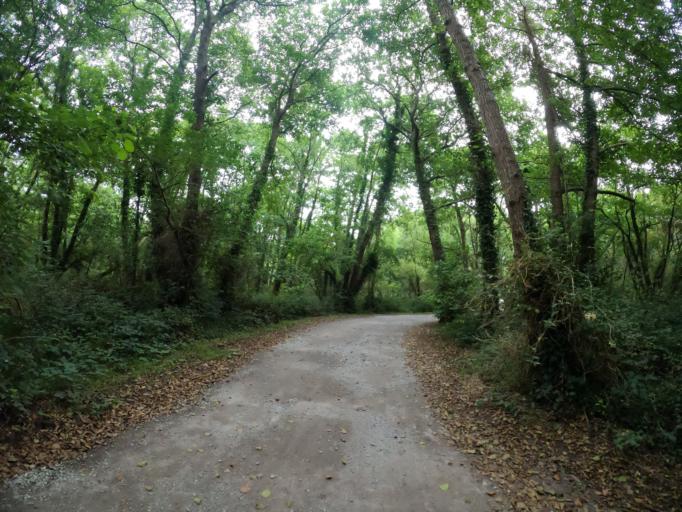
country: FR
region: Aquitaine
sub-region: Departement des Landes
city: Leon
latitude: 43.8863
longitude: -1.3078
